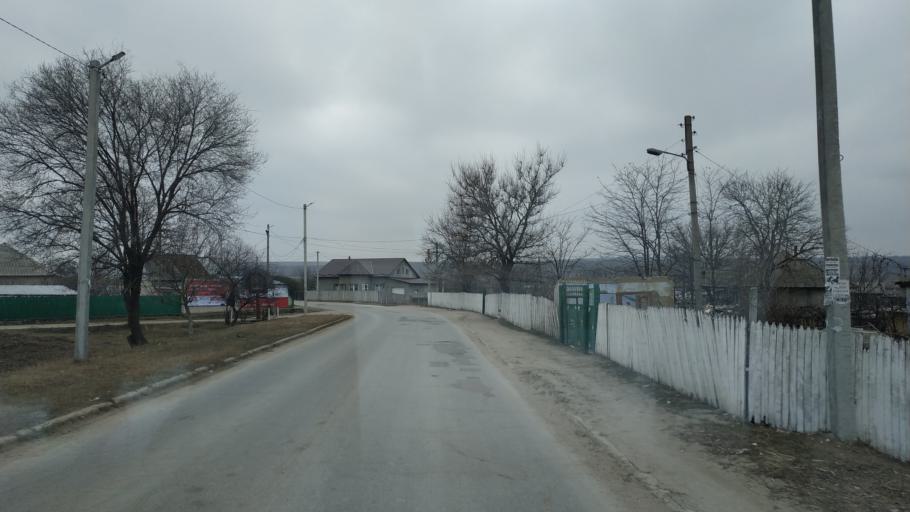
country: MD
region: Hincesti
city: Hincesti
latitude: 46.8768
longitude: 28.4051
